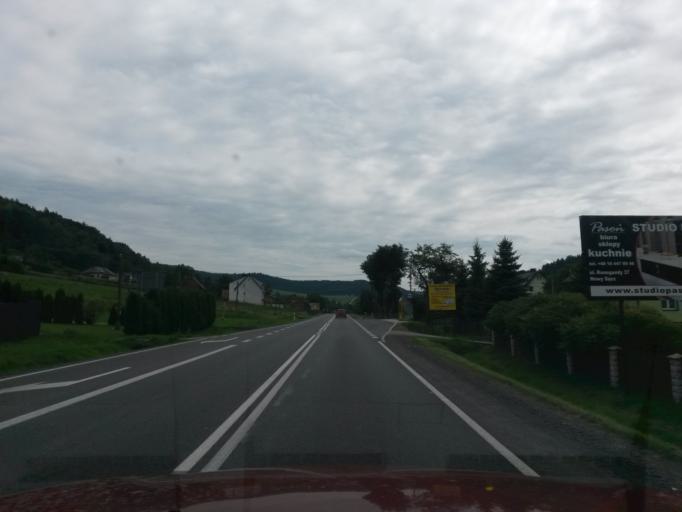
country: PL
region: Lesser Poland Voivodeship
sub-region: Powiat nowosadecki
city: Labowa
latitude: 49.5050
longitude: 20.8946
